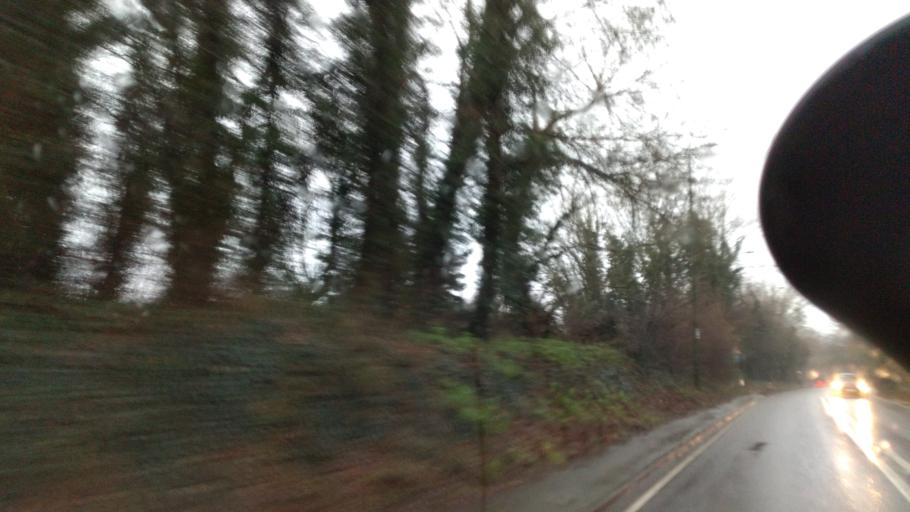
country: GB
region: England
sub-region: West Sussex
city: Arundel
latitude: 50.8533
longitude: -0.5643
